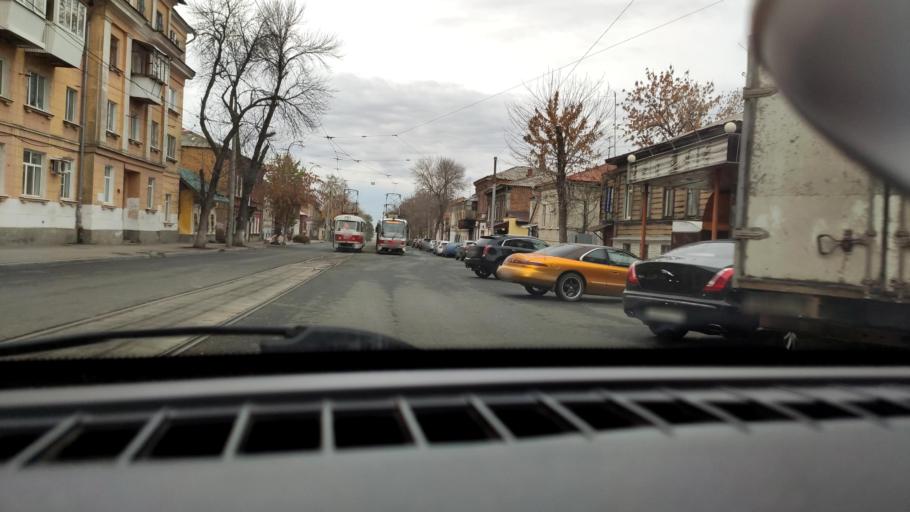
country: RU
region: Samara
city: Samara
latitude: 53.1842
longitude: 50.0916
